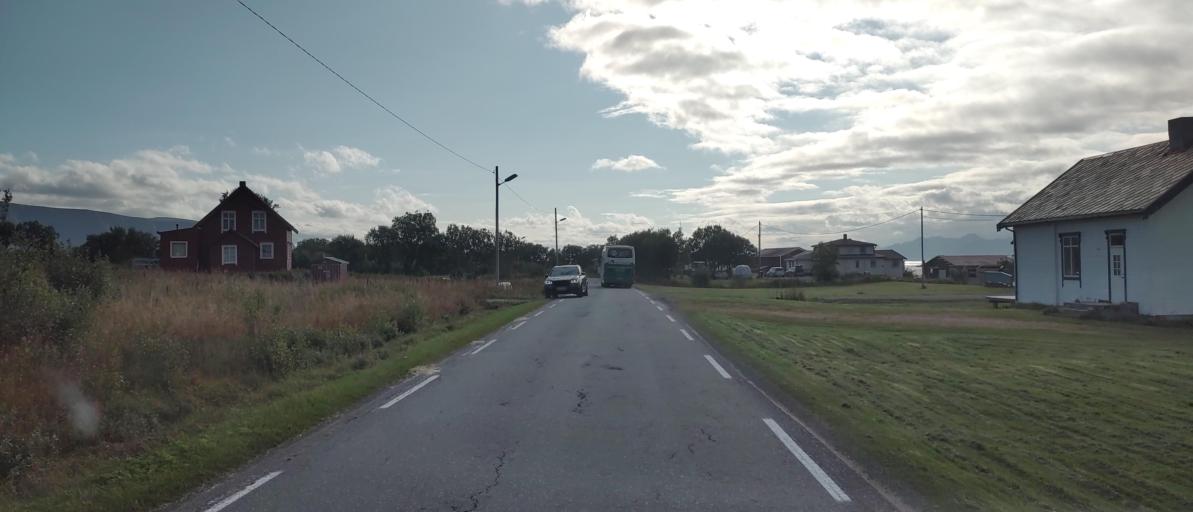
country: NO
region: Nordland
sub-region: Sortland
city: Sortland
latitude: 69.0482
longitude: 15.5193
